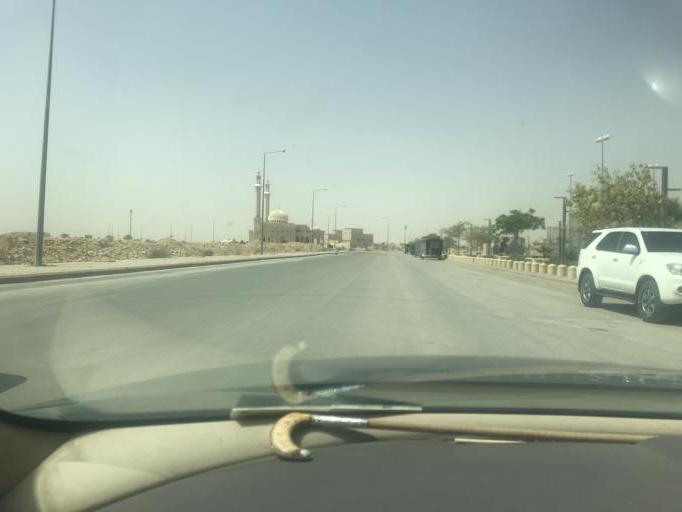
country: SA
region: Ar Riyad
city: Riyadh
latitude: 24.7882
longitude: 46.5804
